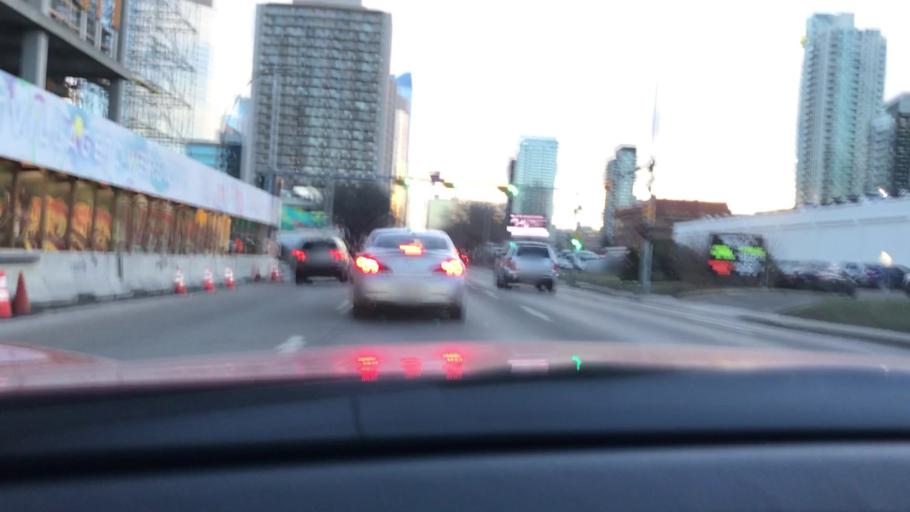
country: CA
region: Alberta
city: Calgary
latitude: 51.0453
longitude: -114.0868
